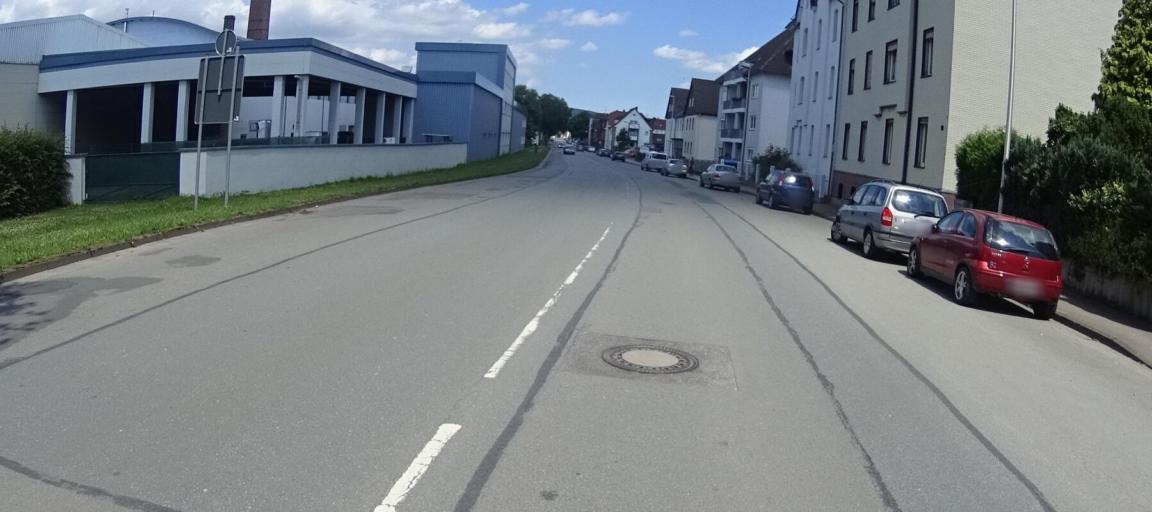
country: DE
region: Lower Saxony
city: Holzminden
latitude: 51.8153
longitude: 9.4489
